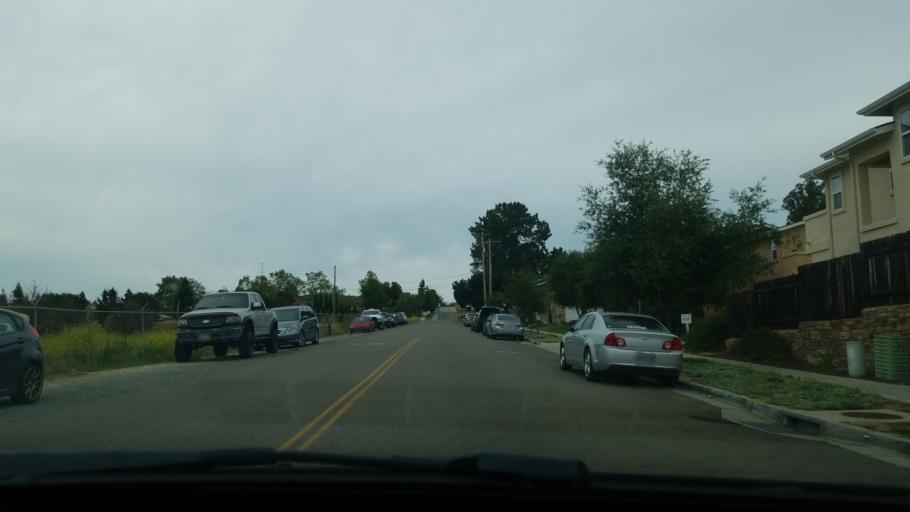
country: US
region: California
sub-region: San Luis Obispo County
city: Nipomo
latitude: 35.0334
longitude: -120.4855
